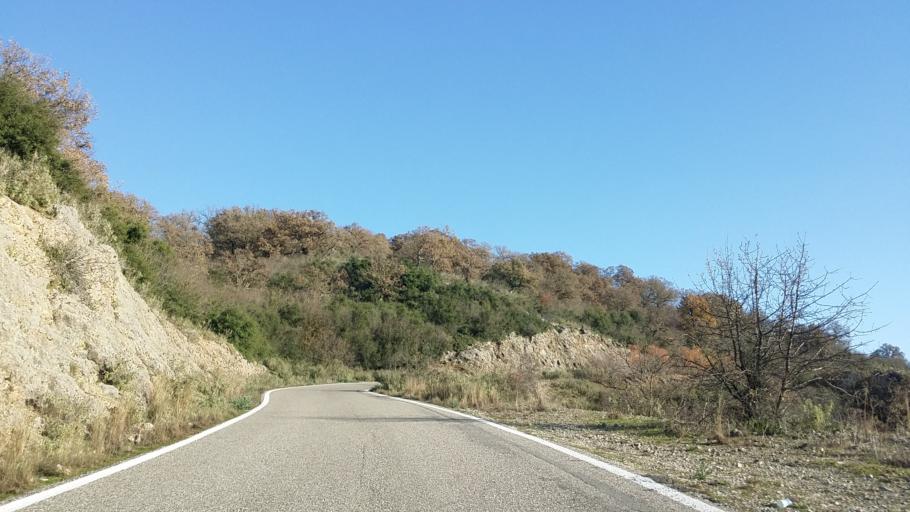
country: GR
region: West Greece
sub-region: Nomos Aitolias kai Akarnanias
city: Fitiai
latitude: 38.6384
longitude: 21.1900
